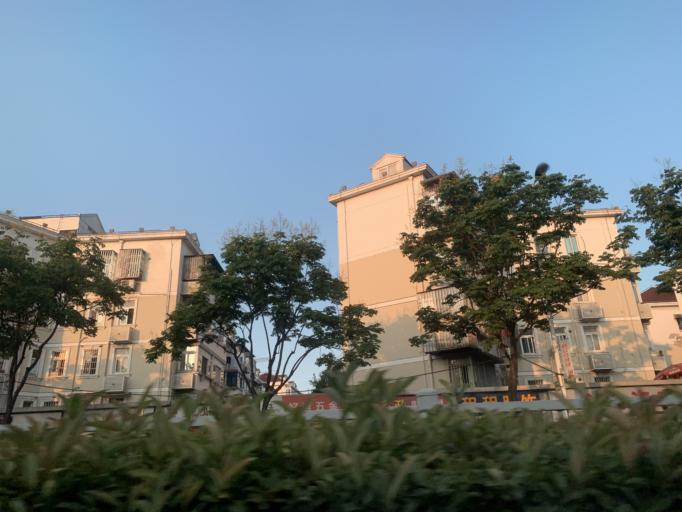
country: CN
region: Shanghai Shi
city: Huamu
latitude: 31.1861
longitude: 121.5501
